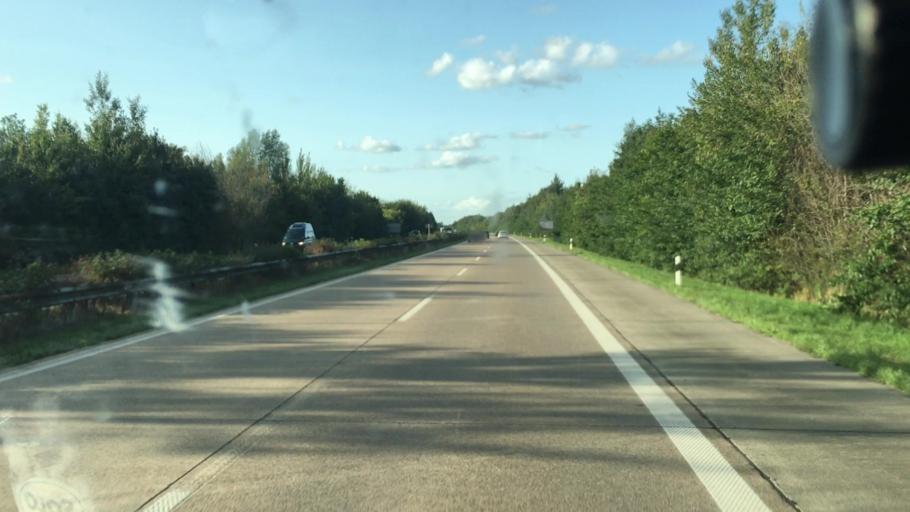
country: DE
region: Lower Saxony
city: Wiefelstede
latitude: 53.3063
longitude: 8.1448
